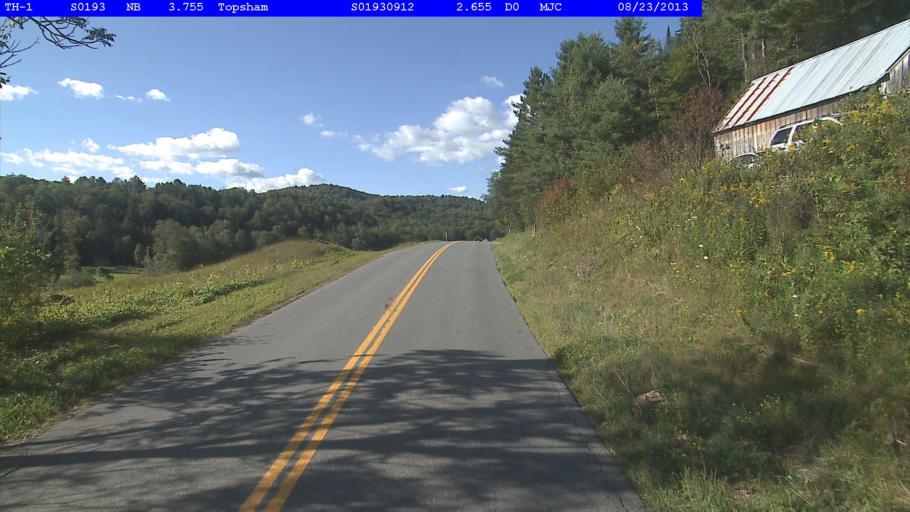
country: US
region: New Hampshire
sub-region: Grafton County
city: Haverhill
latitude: 44.1056
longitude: -72.2325
